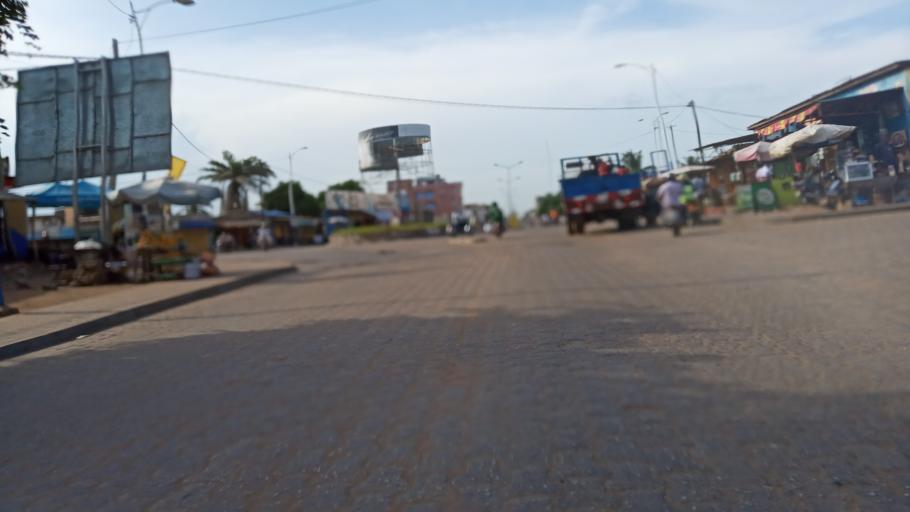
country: TG
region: Maritime
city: Lome
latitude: 6.1617
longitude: 1.2663
